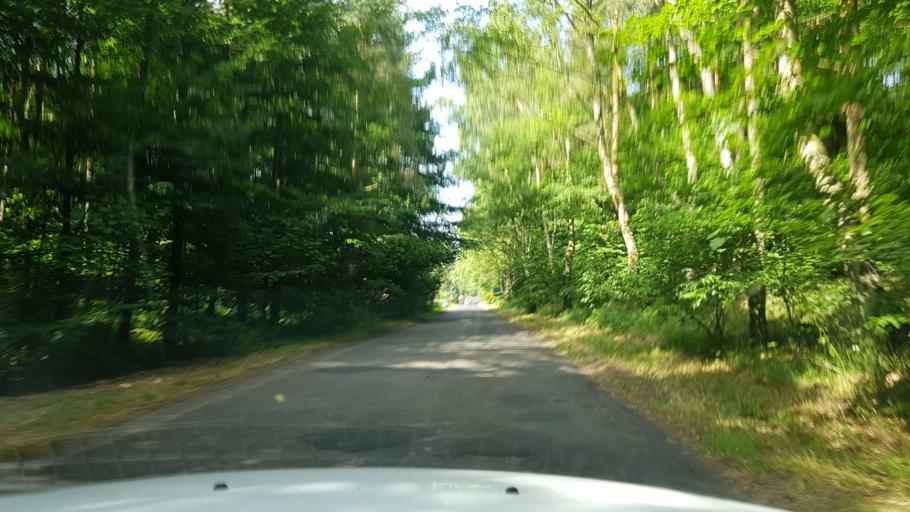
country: PL
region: West Pomeranian Voivodeship
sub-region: Powiat goleniowski
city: Mosty
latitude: 53.5585
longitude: 14.9746
